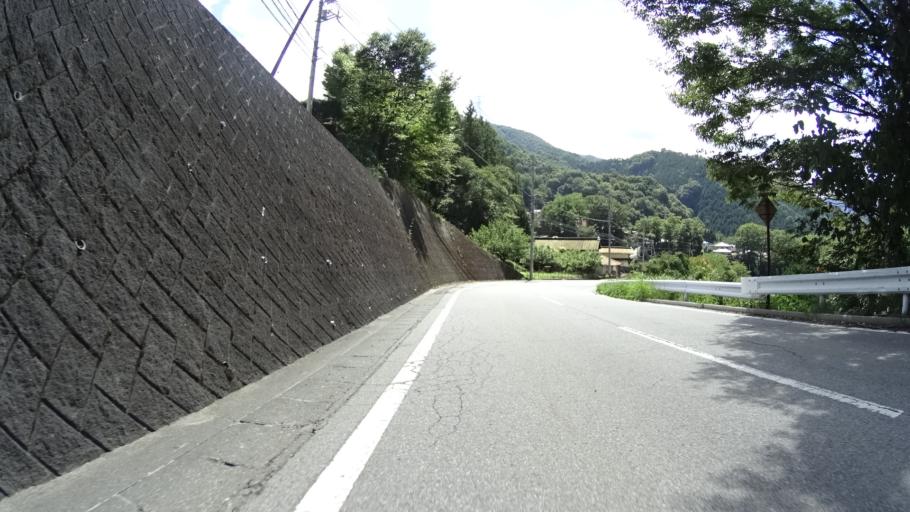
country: JP
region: Yamanashi
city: Enzan
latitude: 35.6421
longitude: 138.8029
